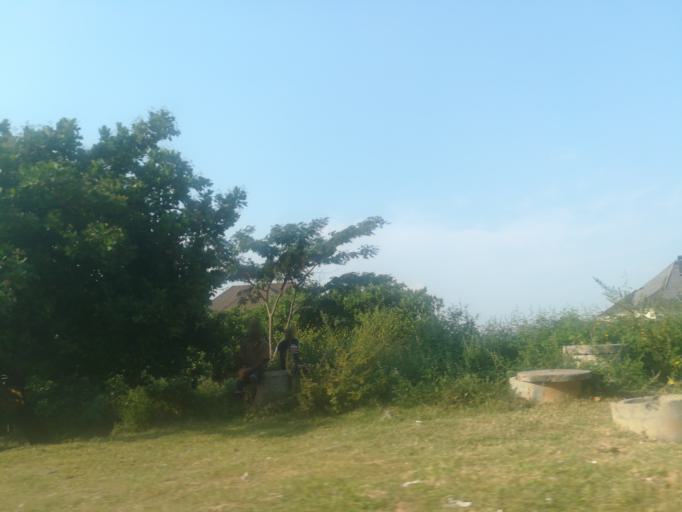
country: NG
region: Abuja Federal Capital Territory
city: Abuja
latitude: 9.0460
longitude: 7.4396
